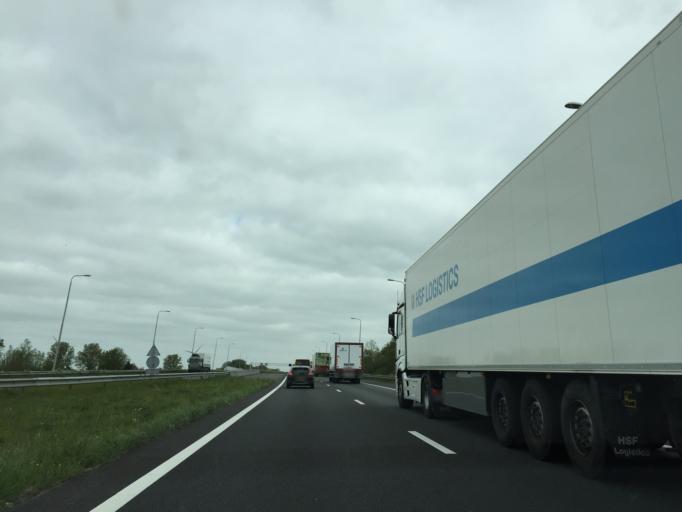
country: NL
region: North Holland
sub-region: Gemeente Hoorn
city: Hoorn
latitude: 52.6182
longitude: 5.0040
